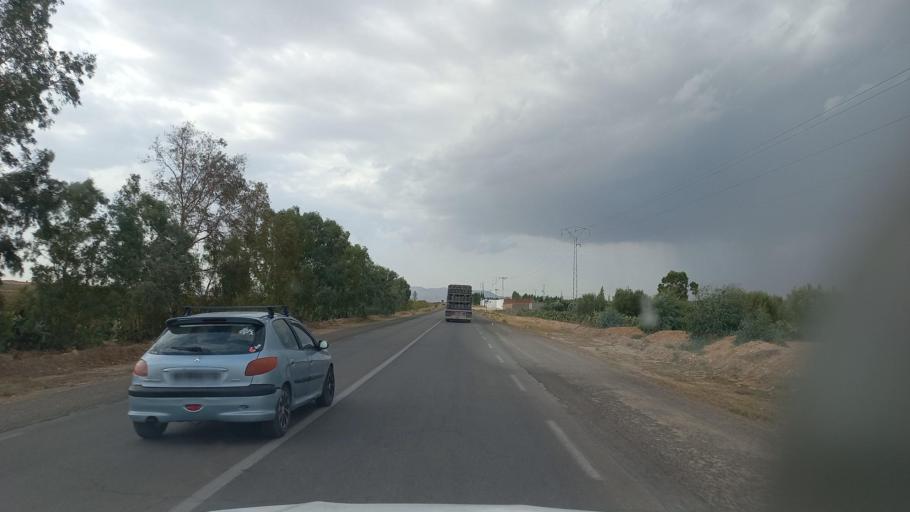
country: TN
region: Al Qasrayn
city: Sbiba
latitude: 35.3091
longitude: 9.0858
